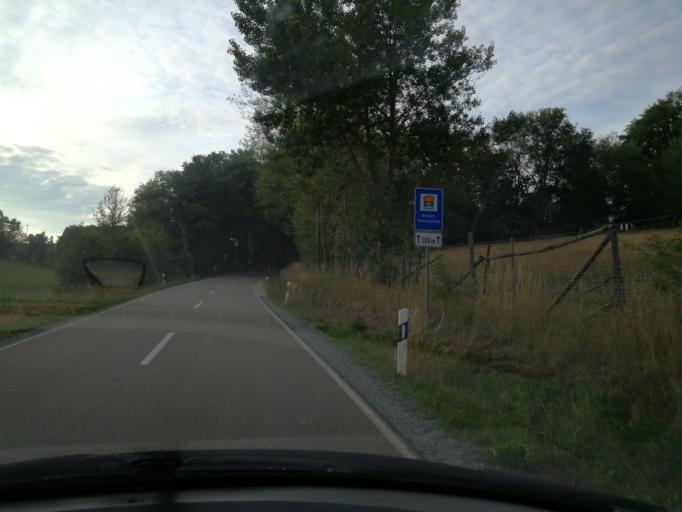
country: DE
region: Bavaria
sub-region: Lower Bavaria
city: Falkenfels
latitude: 49.0486
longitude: 12.5948
